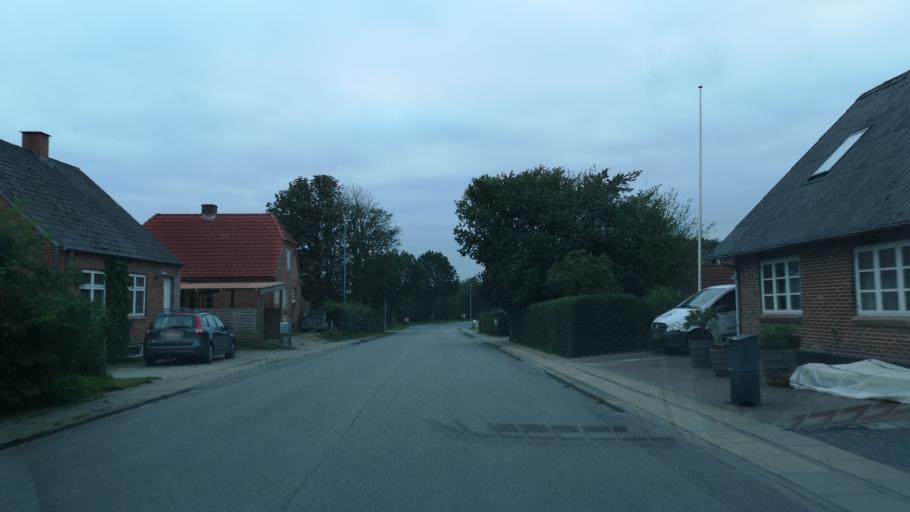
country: DK
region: Central Jutland
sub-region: Ringkobing-Skjern Kommune
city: Videbaek
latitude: 56.0664
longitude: 8.6009
